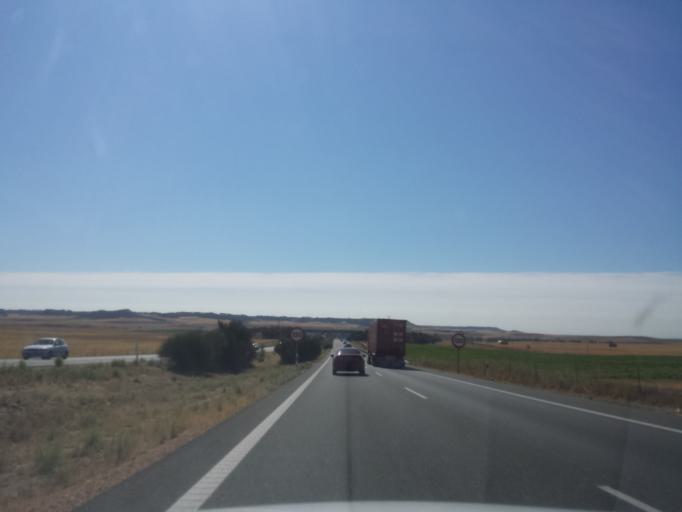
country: ES
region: Castille and Leon
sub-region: Provincia de Valladolid
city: Marzales
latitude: 41.6069
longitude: -5.1408
